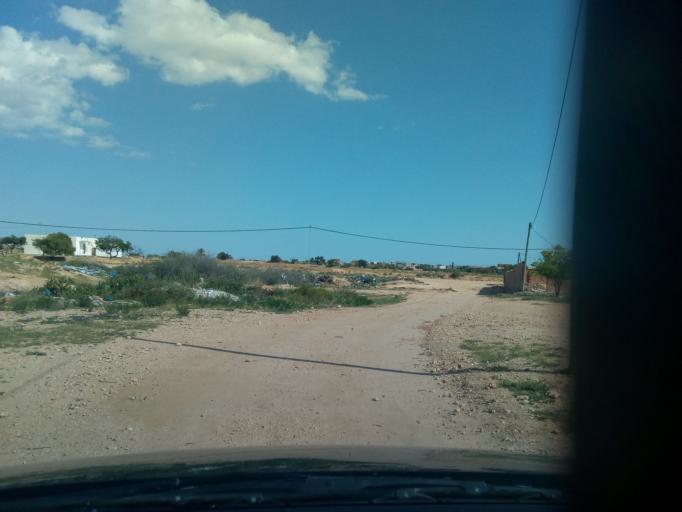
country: TN
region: Safaqis
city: Sfax
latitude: 34.7270
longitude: 10.6042
